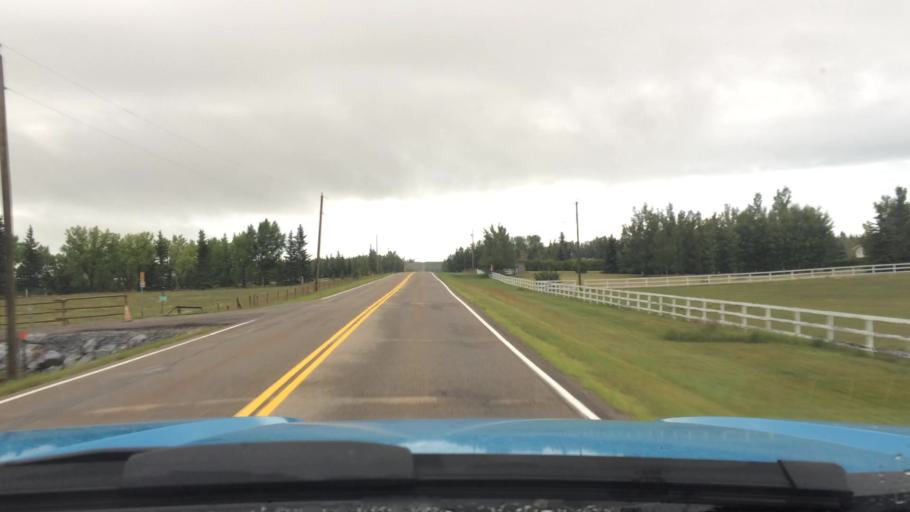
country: CA
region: Alberta
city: Airdrie
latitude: 51.2012
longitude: -114.1412
